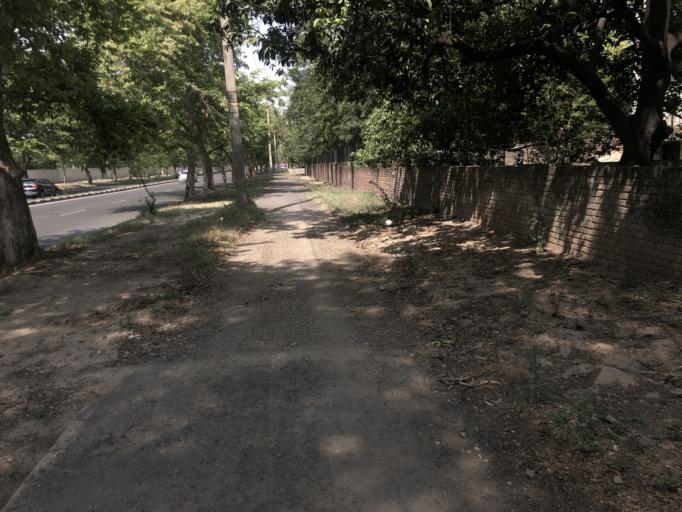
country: IN
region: Chandigarh
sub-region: Chandigarh
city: Chandigarh
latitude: 30.6997
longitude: 76.7691
